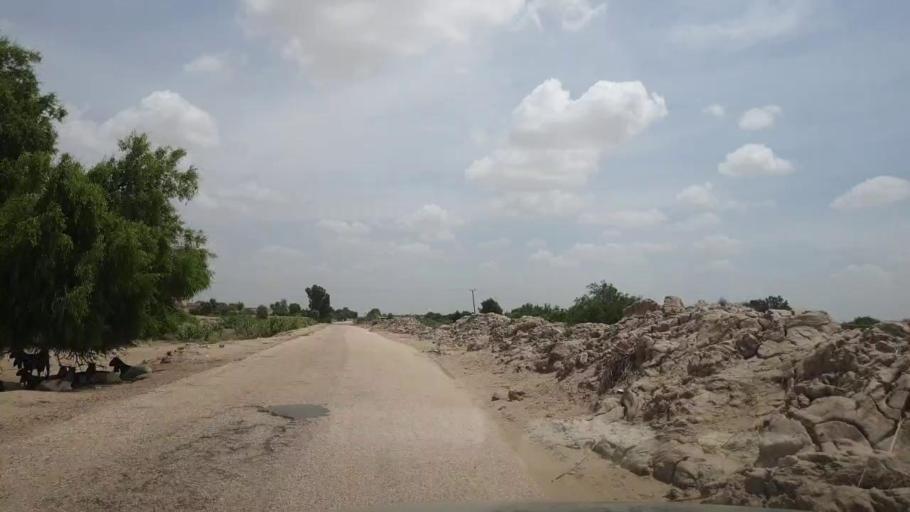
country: PK
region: Sindh
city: Kot Diji
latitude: 27.2124
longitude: 69.1134
